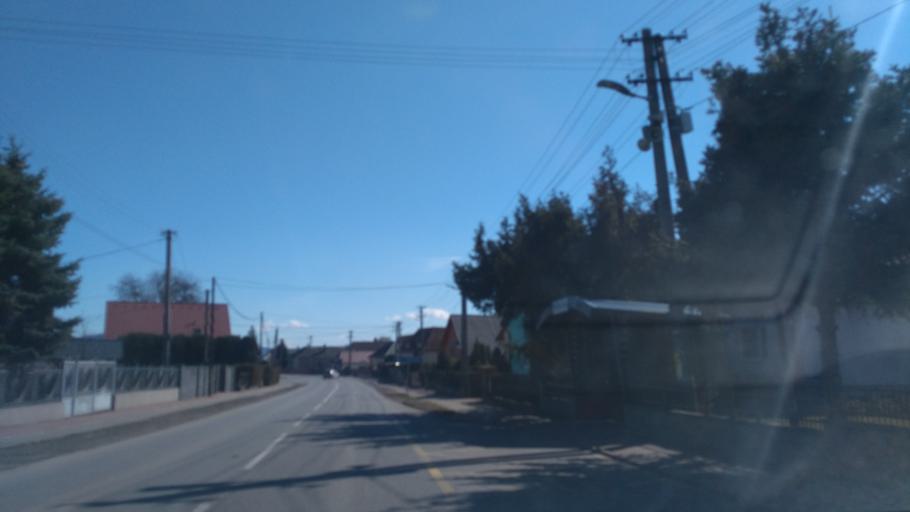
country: SK
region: Kosicky
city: Kosice
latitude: 48.6413
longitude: 21.2921
